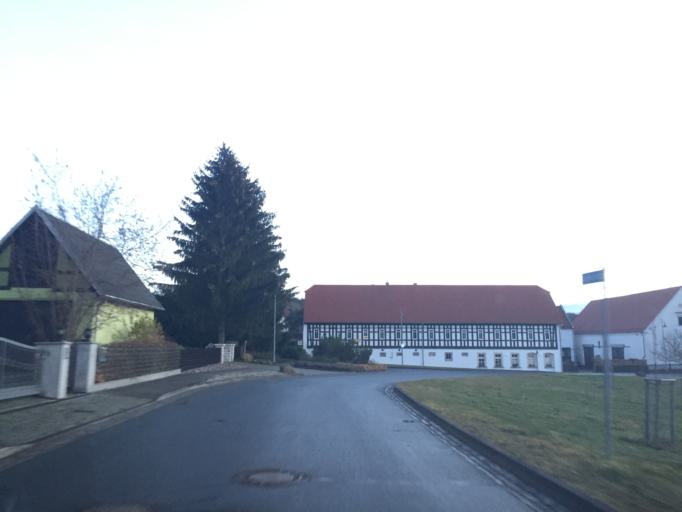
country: DE
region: Thuringia
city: Heyersdorf
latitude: 50.8672
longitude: 12.3312
